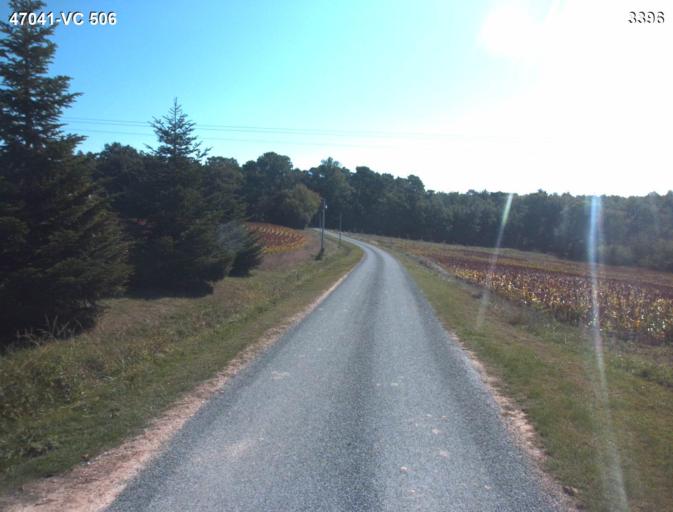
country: FR
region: Aquitaine
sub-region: Departement du Lot-et-Garonne
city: Port-Sainte-Marie
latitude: 44.1890
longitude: 0.3840
